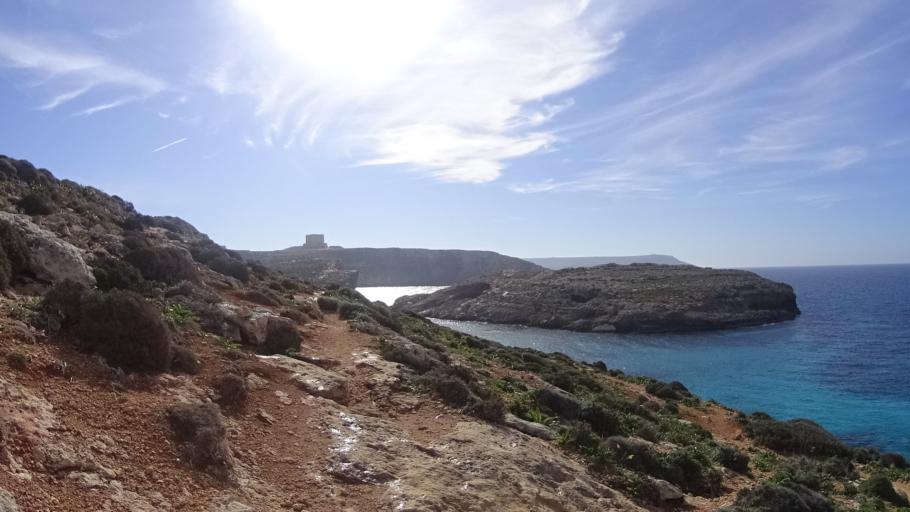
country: MT
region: Il-Qala
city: Qala
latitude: 36.0127
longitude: 14.3248
